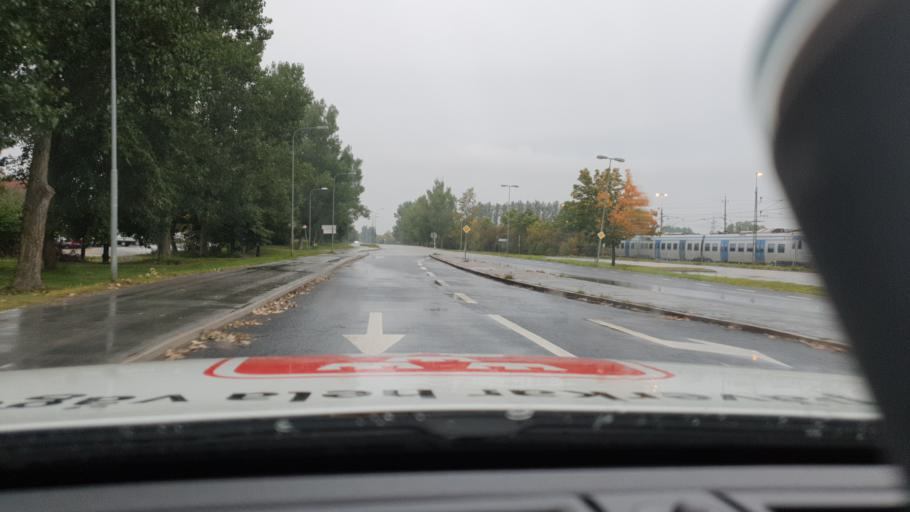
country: SE
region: Stockholm
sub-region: Sigtuna Kommun
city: Marsta
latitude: 59.6304
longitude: 17.8603
